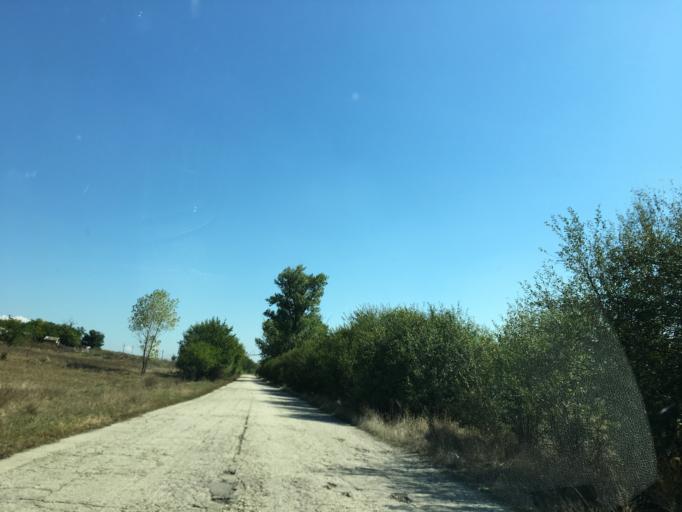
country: BG
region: Pleven
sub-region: Obshtina Knezha
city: Knezha
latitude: 43.5381
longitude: 24.1153
